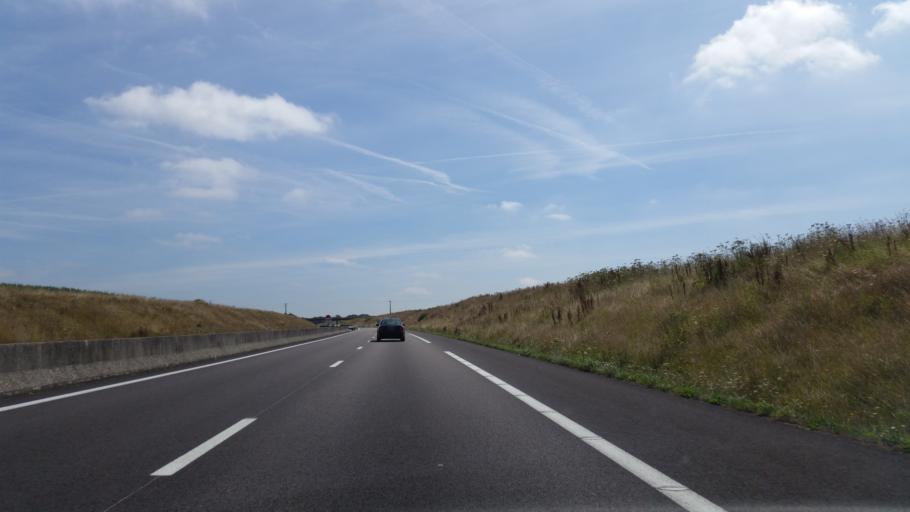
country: FR
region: Haute-Normandie
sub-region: Departement de la Seine-Maritime
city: Gaillefontaine
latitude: 49.7387
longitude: 1.6112
